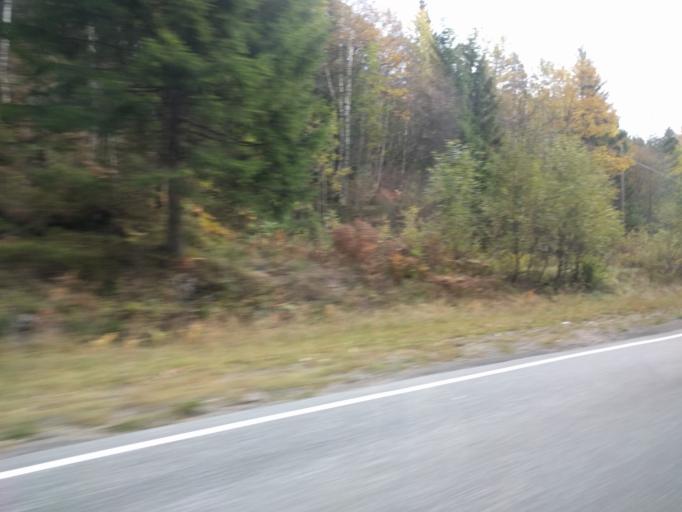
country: NO
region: Vest-Agder
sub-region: Songdalen
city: Nodeland
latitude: 58.3003
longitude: 7.8215
